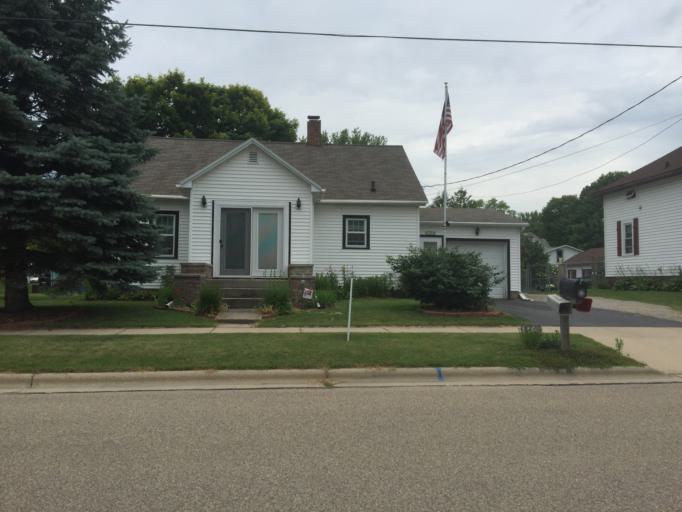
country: US
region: Wisconsin
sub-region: Oconto County
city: Gillett
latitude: 44.8942
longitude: -88.3096
